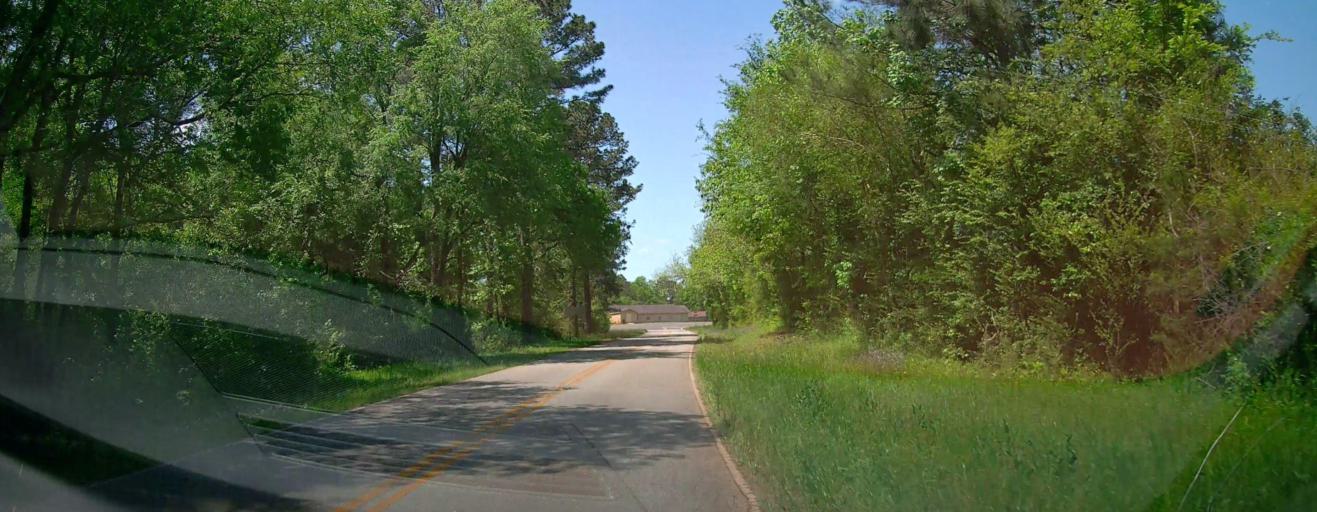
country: US
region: Georgia
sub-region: Jasper County
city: Monticello
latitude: 33.2824
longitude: -83.7120
